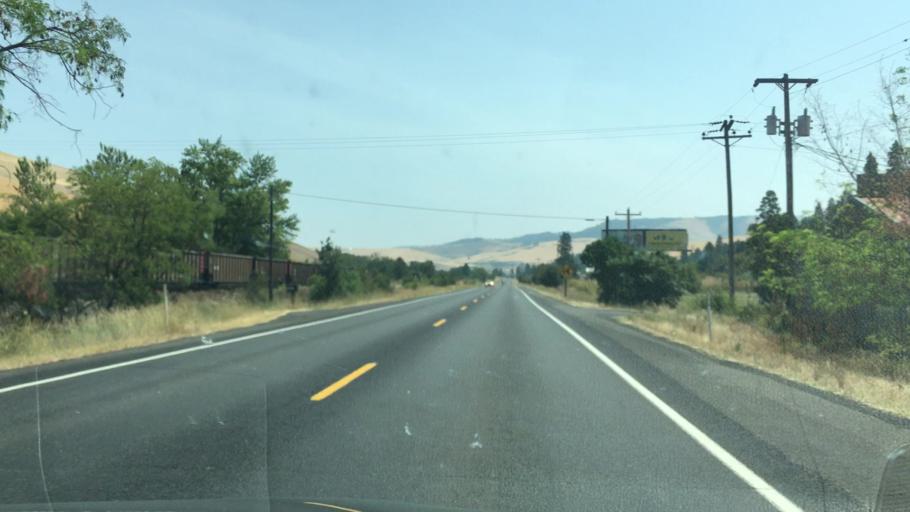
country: US
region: Idaho
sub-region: Nez Perce County
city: Lapwai
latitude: 46.3722
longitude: -116.7051
